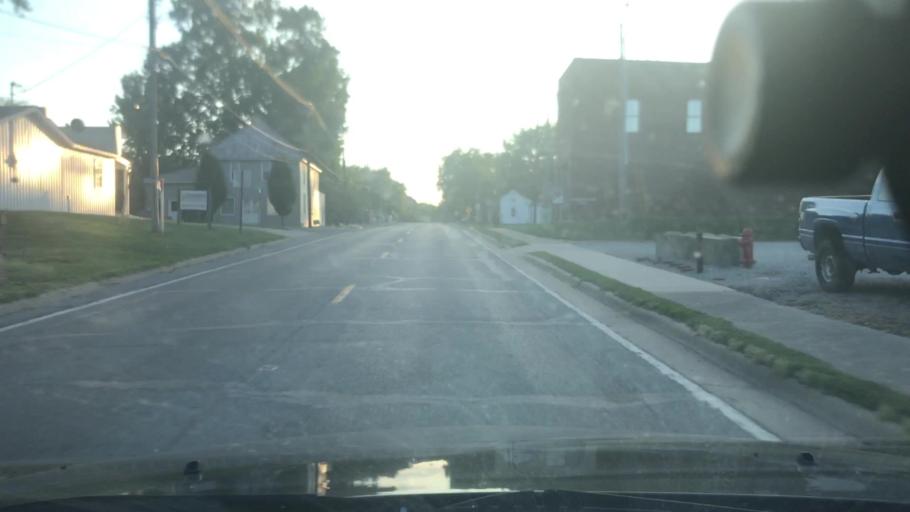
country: US
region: Illinois
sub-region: Washington County
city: Okawville
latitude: 38.4360
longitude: -89.5480
